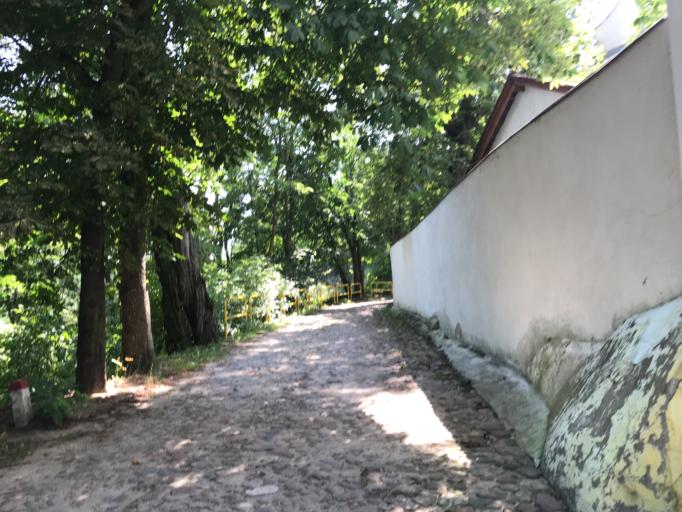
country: PL
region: Kujawsko-Pomorskie
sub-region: Powiat golubsko-dobrzynski
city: Zbojno
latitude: 53.0017
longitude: 19.2138
